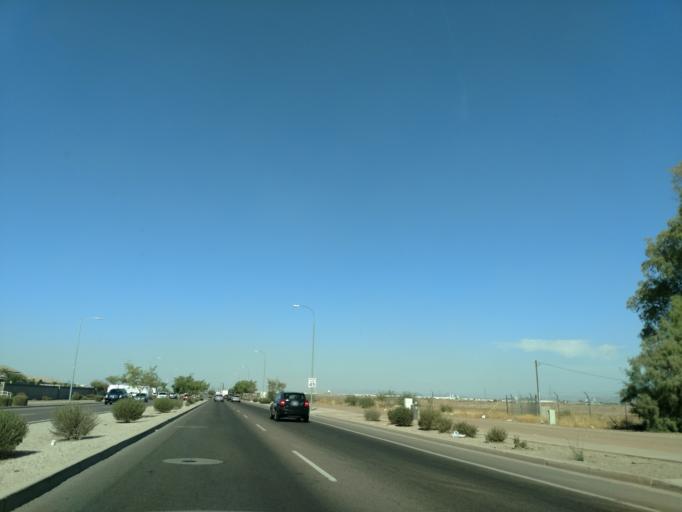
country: US
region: Arizona
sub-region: Maricopa County
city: Laveen
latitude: 33.3973
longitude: -112.1683
